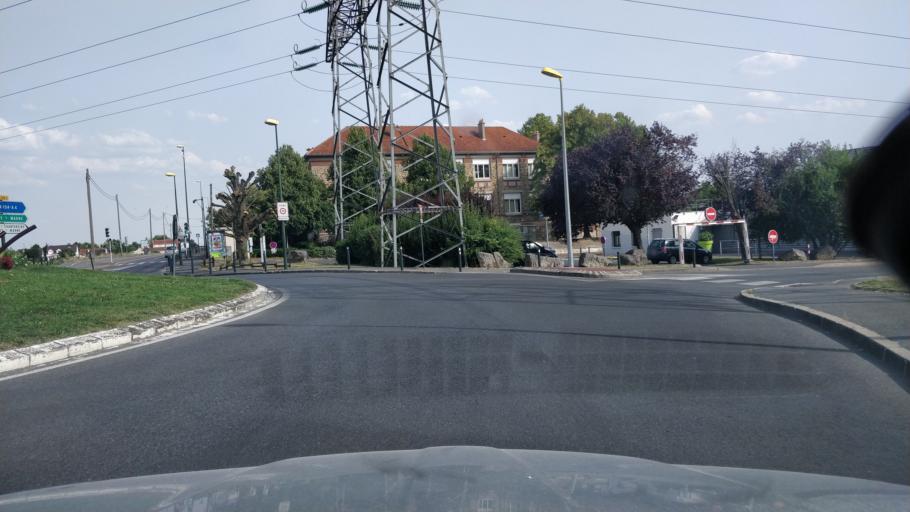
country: FR
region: Ile-de-France
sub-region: Departement de Seine-et-Marne
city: Brou-sur-Chantereine
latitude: 48.8882
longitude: 2.6139
